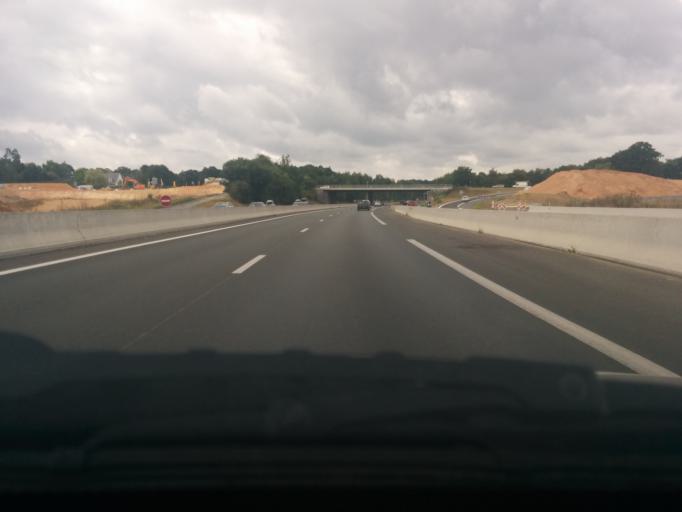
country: FR
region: Pays de la Loire
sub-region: Departement de Maine-et-Loire
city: Les Ponts-de-Ce
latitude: 47.4016
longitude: -0.5119
